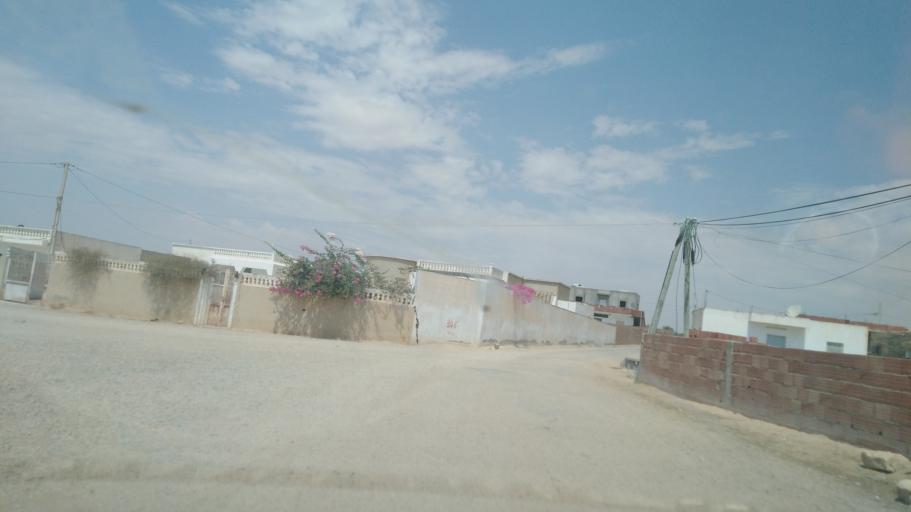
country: TN
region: Safaqis
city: Sfax
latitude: 34.7431
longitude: 10.5607
